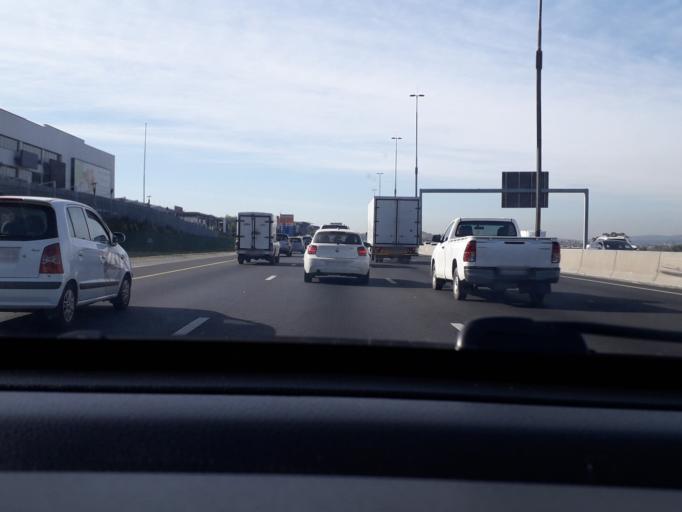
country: ZA
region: Gauteng
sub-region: City of Johannesburg Metropolitan Municipality
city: Modderfontein
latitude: -26.0646
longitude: 28.1090
